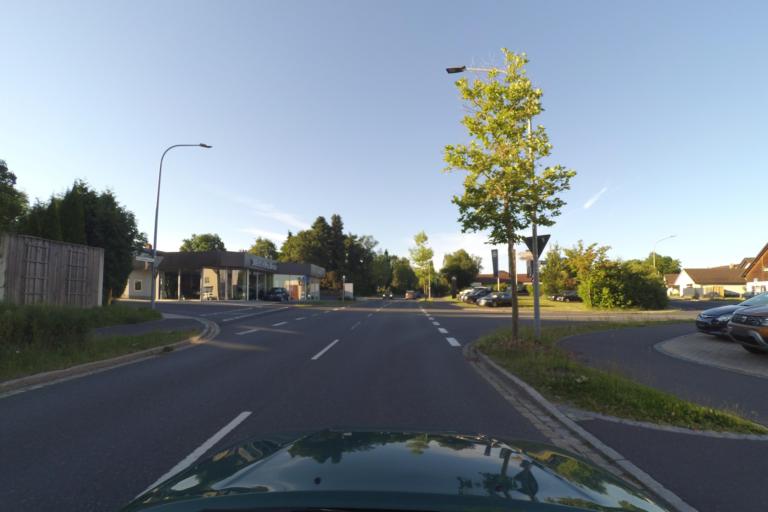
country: DE
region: Bavaria
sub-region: Upper Palatinate
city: Tirschenreuth
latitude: 49.8731
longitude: 12.3414
